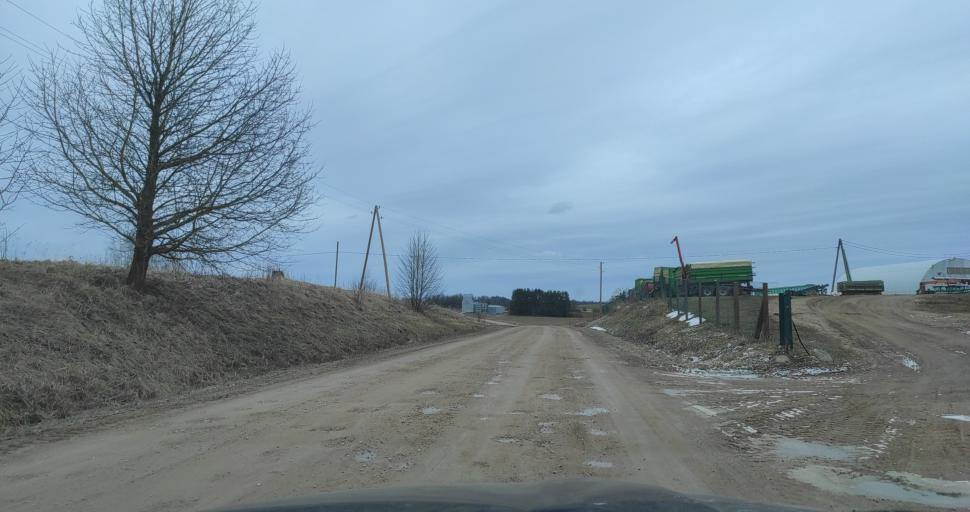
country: LV
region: Tukuma Rajons
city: Tukums
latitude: 57.0617
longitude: 23.0305
